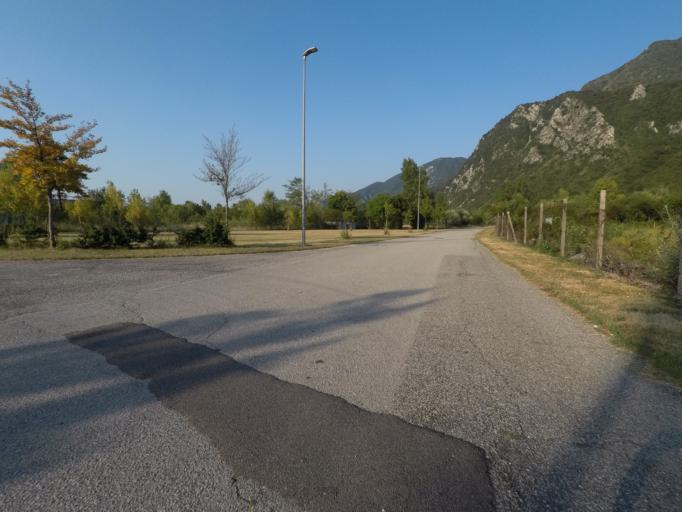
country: IT
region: Friuli Venezia Giulia
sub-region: Provincia di Udine
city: Trasaghis
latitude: 46.2777
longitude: 13.0647
